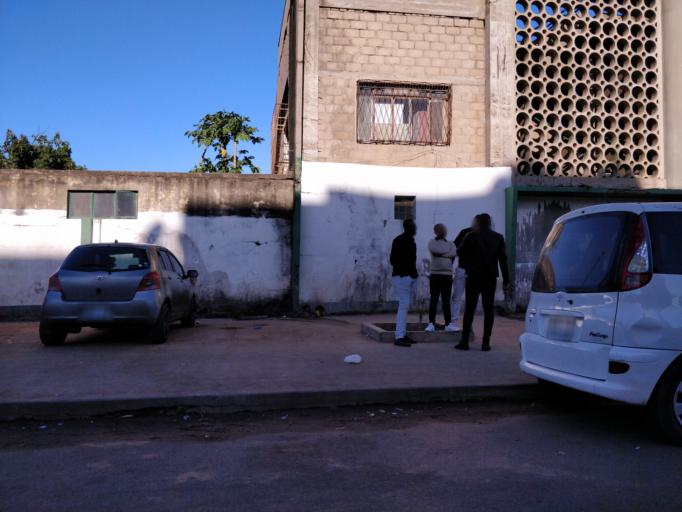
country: MZ
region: Maputo City
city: Maputo
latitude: -25.9674
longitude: 32.5659
